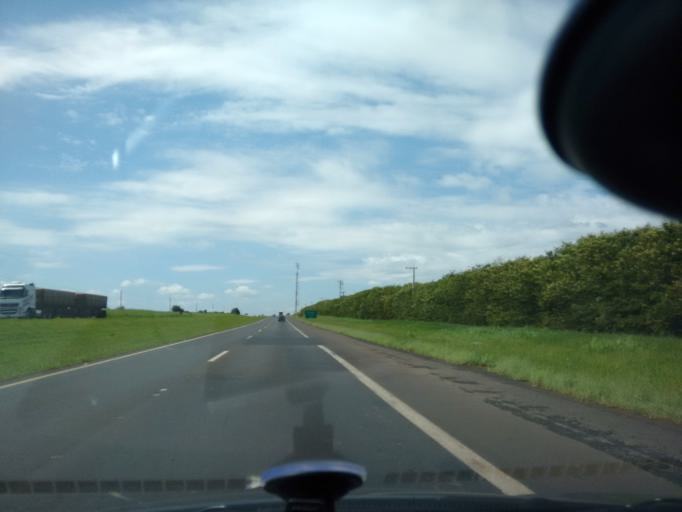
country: BR
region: Sao Paulo
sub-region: Araraquara
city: Araraquara
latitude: -21.8588
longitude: -48.1223
